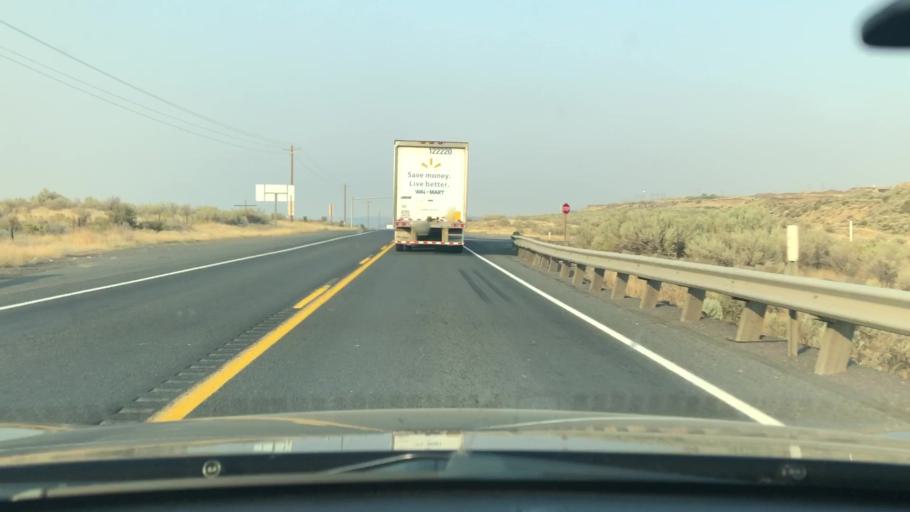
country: US
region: Oregon
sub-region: Umatilla County
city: Stanfield
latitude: 45.9156
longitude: -119.1344
